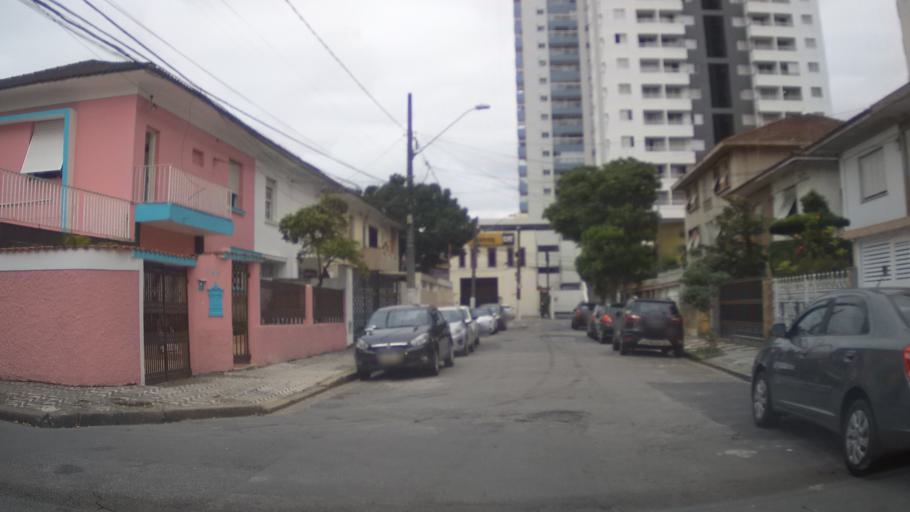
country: BR
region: Sao Paulo
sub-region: Santos
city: Santos
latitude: -23.9569
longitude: -46.3207
